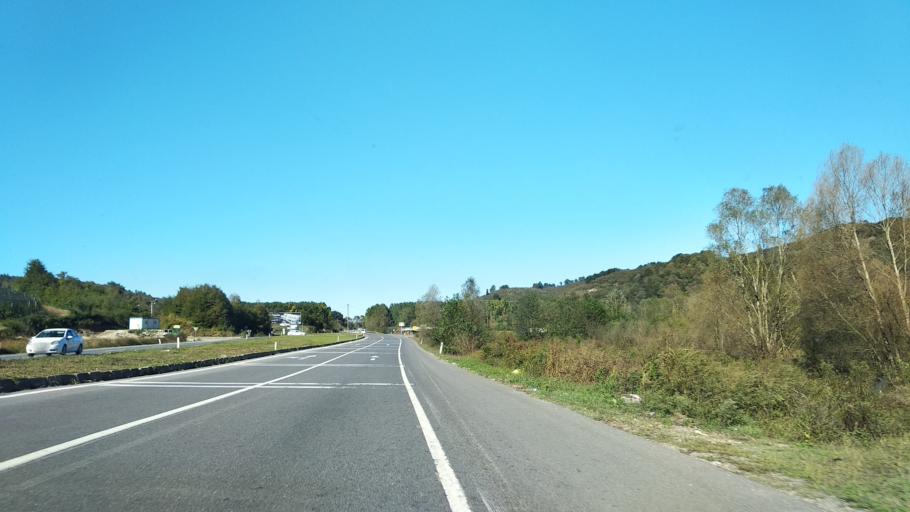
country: TR
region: Sakarya
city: Karasu
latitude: 41.0526
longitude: 30.6350
